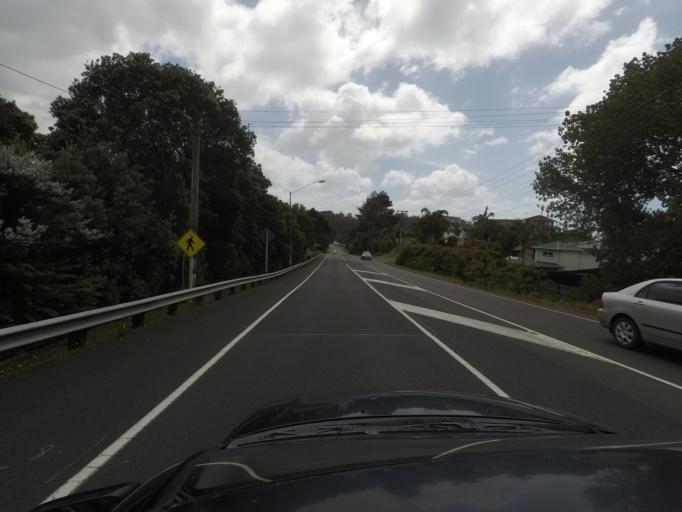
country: NZ
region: Auckland
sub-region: Auckland
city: Rothesay Bay
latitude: -36.5673
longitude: 174.6924
